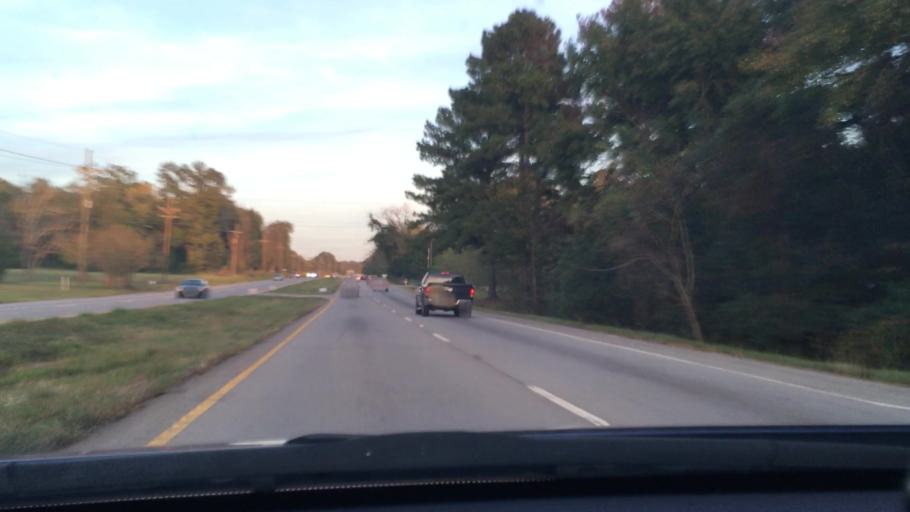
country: US
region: South Carolina
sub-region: Richland County
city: Hopkins
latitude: 33.9483
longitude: -80.8634
